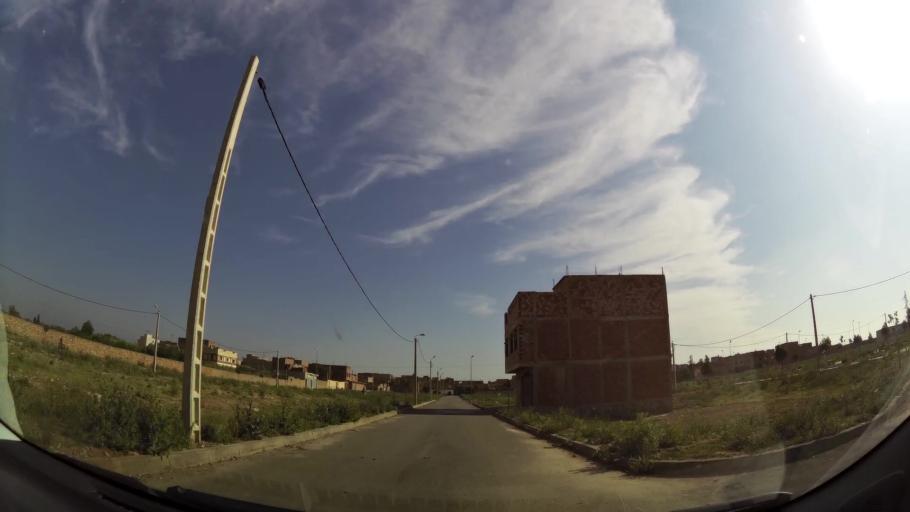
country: MA
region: Oriental
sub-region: Oujda-Angad
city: Oujda
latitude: 34.7230
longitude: -1.8832
